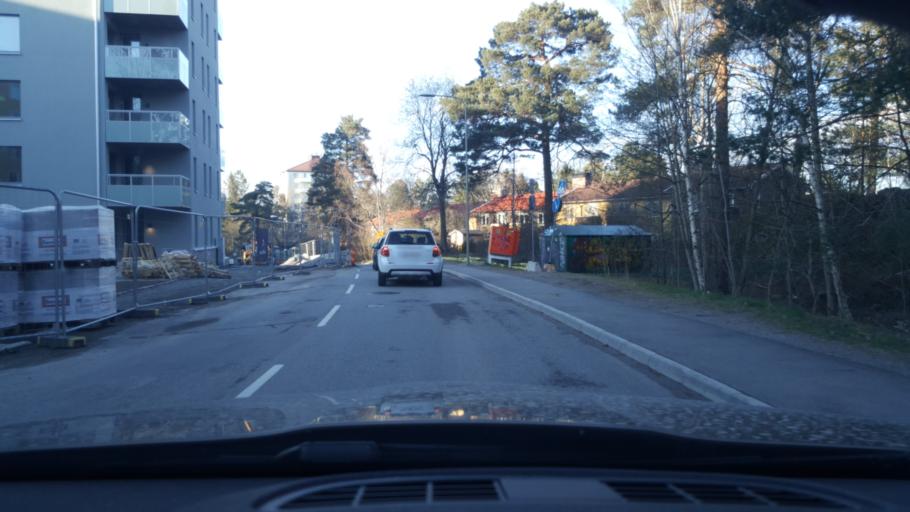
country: SE
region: Stockholm
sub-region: Stockholms Kommun
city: Arsta
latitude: 59.2648
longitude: 18.0565
